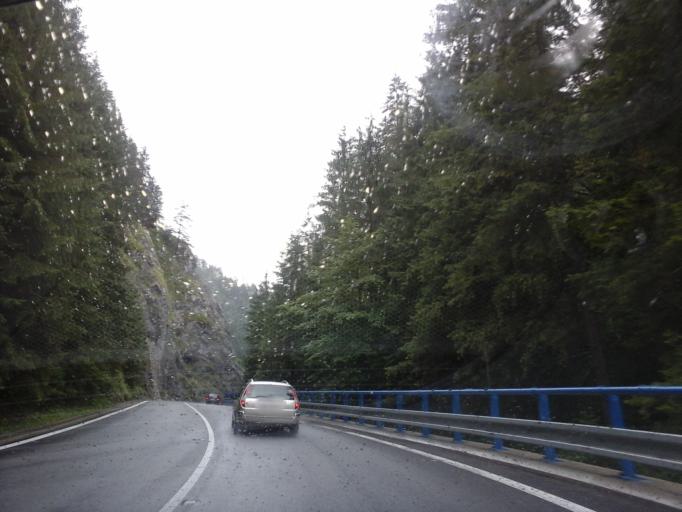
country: SK
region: Presovsky
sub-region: Okres Poprad
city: Poprad
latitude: 48.9317
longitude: 20.2861
